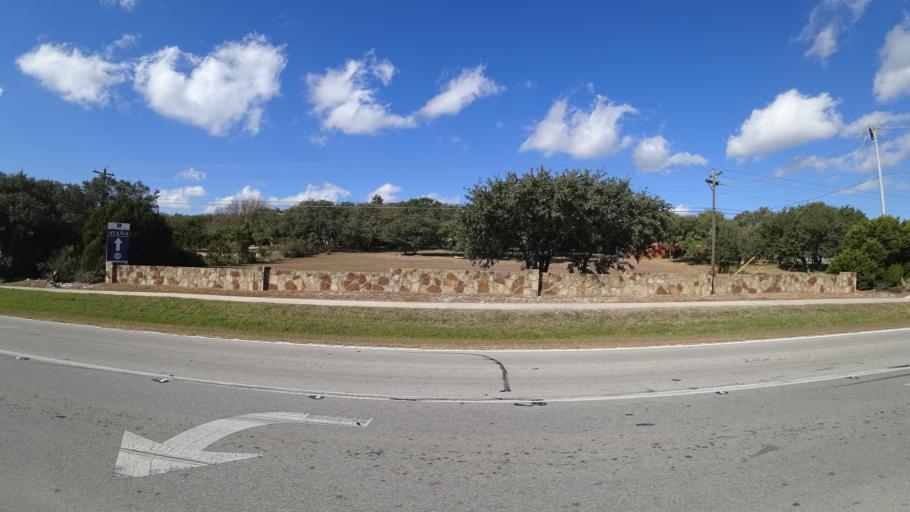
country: US
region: Texas
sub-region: Travis County
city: Shady Hollow
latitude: 30.2187
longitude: -97.8943
